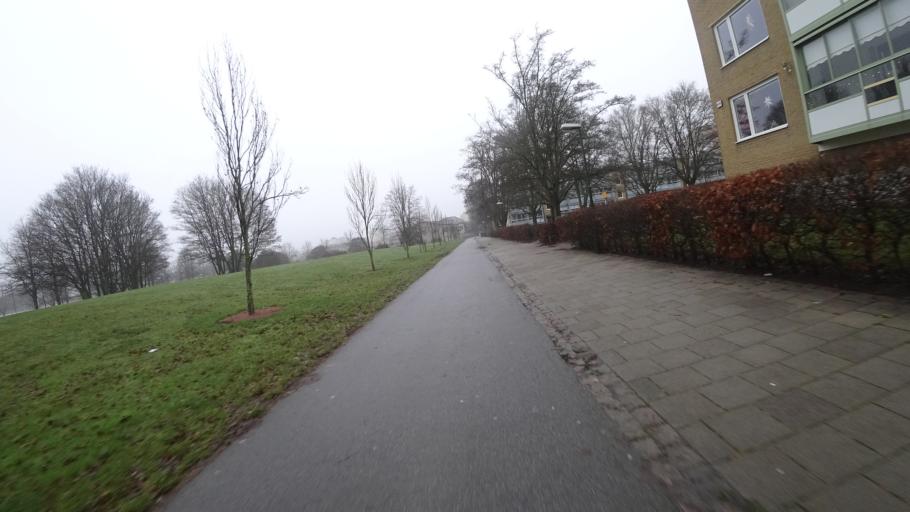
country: SE
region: Skane
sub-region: Malmo
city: Malmoe
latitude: 55.5820
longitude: 12.9937
